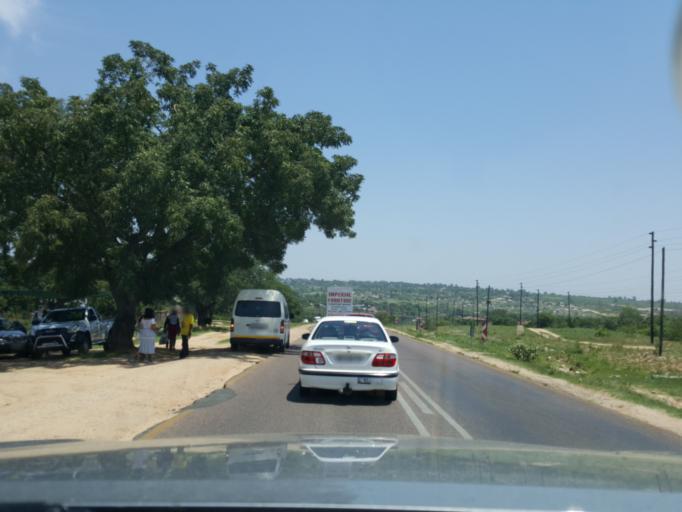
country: ZA
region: Limpopo
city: Thulamahashi
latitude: -24.7937
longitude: 31.0823
